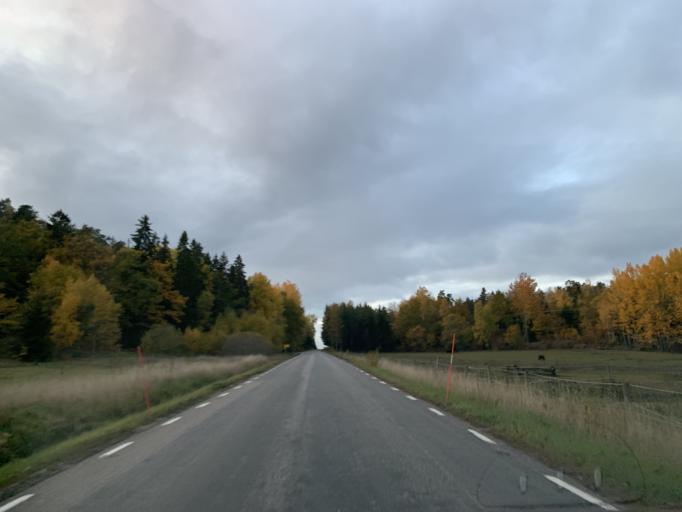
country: SE
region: Stockholm
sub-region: Nynashamns Kommun
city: Osmo
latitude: 58.9332
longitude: 17.7645
